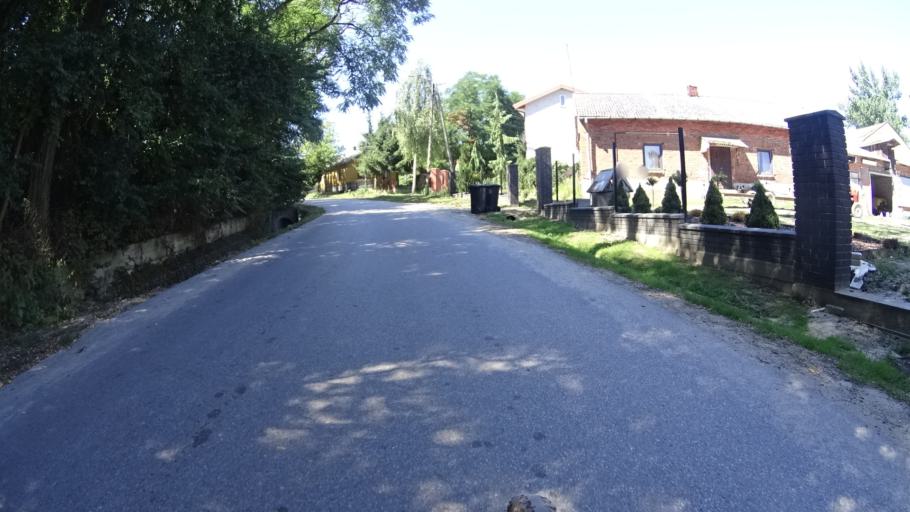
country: PL
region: Masovian Voivodeship
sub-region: Powiat bialobrzeski
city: Bialobrzegi
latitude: 51.6678
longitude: 20.9164
